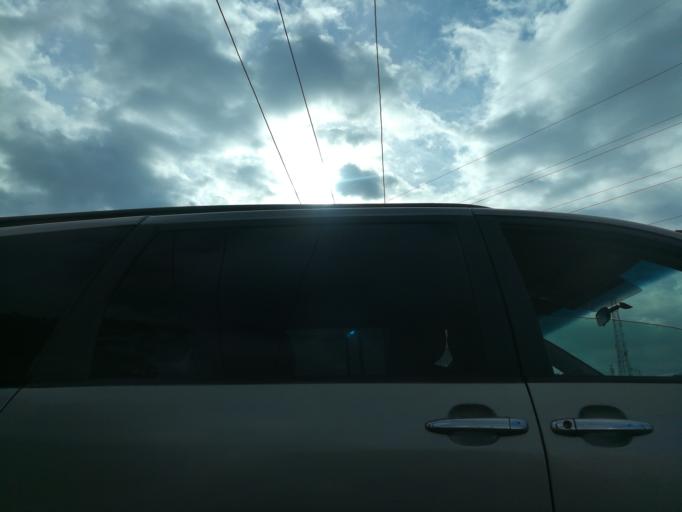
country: NG
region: Lagos
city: Ebute Ikorodu
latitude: 6.6192
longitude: 3.4753
